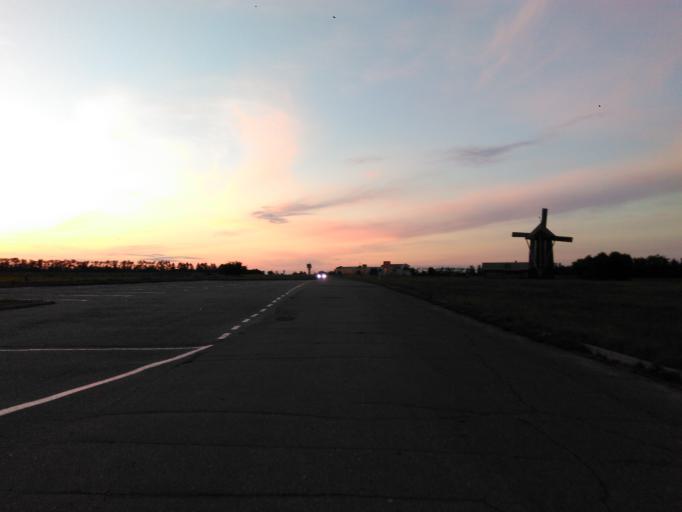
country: RU
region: Penza
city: Lermontovo
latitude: 52.9954
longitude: 43.6732
